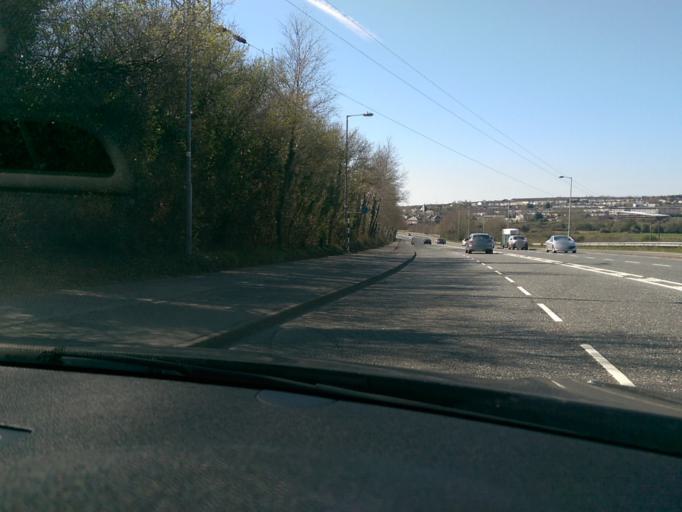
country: IE
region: Connaught
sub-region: County Galway
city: Gaillimh
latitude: 53.2918
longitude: -9.0243
